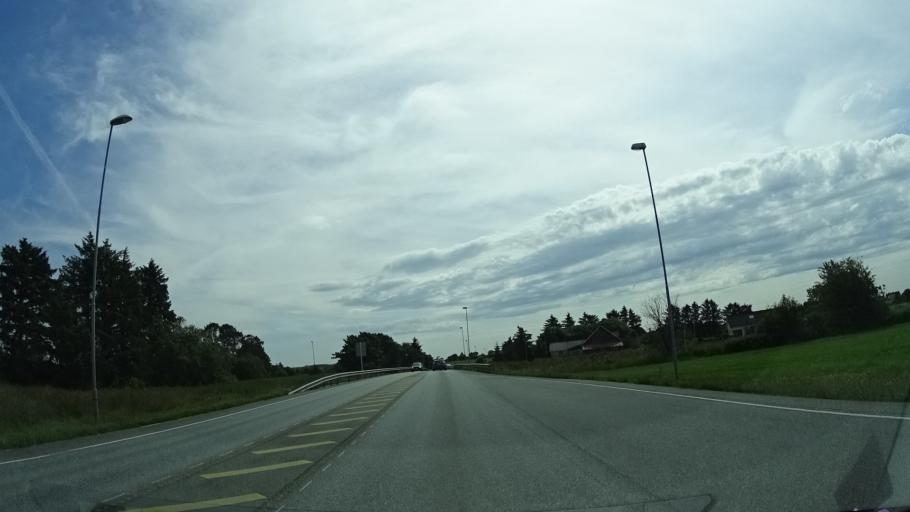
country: NO
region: Rogaland
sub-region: Randaberg
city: Randaberg
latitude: 59.0077
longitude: 5.6402
